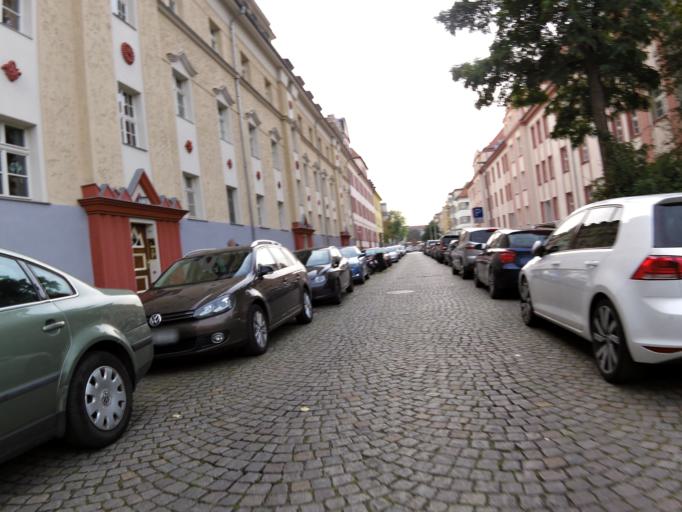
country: DE
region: Saxony
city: Leipzig
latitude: 51.3301
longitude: 12.4097
